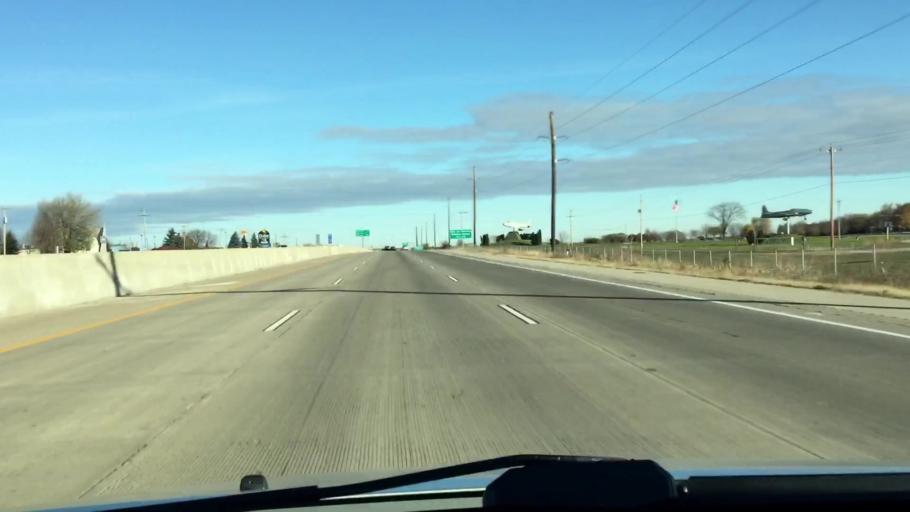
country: US
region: Wisconsin
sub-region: Winnebago County
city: Oshkosh
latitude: 43.9795
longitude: -88.5826
